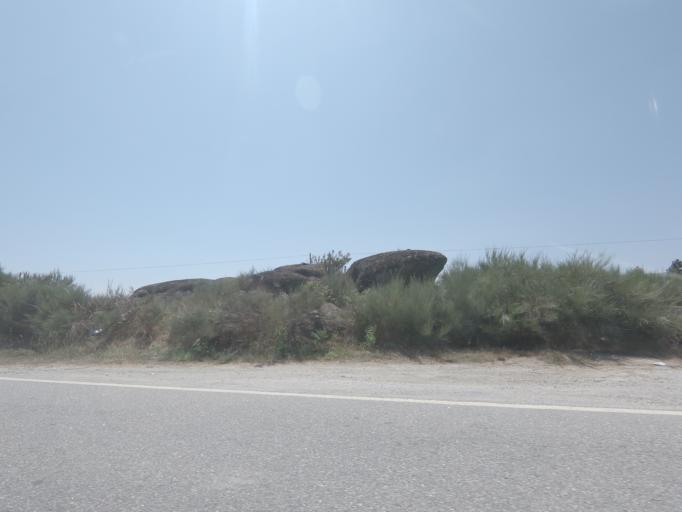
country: PT
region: Viseu
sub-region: Castro Daire
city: Castro Daire
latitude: 40.9686
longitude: -7.8840
